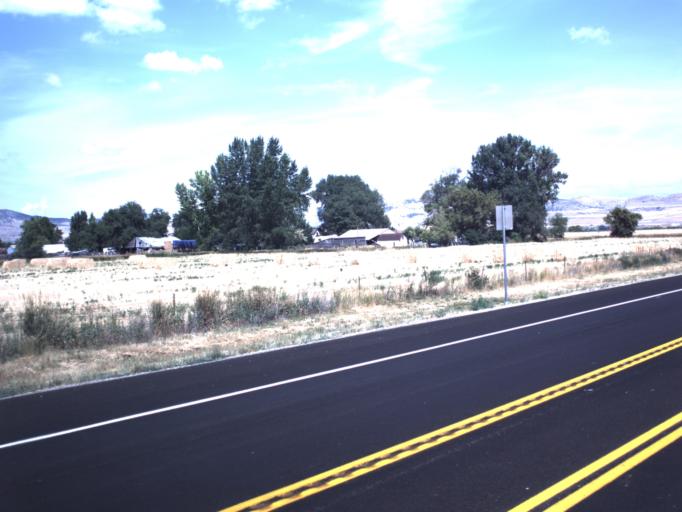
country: US
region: Utah
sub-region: Box Elder County
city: Garland
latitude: 41.7854
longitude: -112.1281
